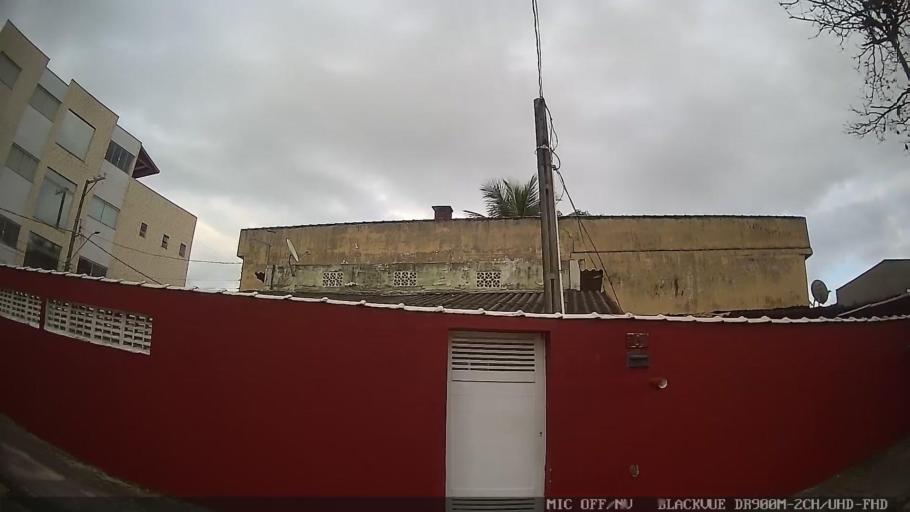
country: BR
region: Sao Paulo
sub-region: Itanhaem
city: Itanhaem
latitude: -24.1924
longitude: -46.8135
